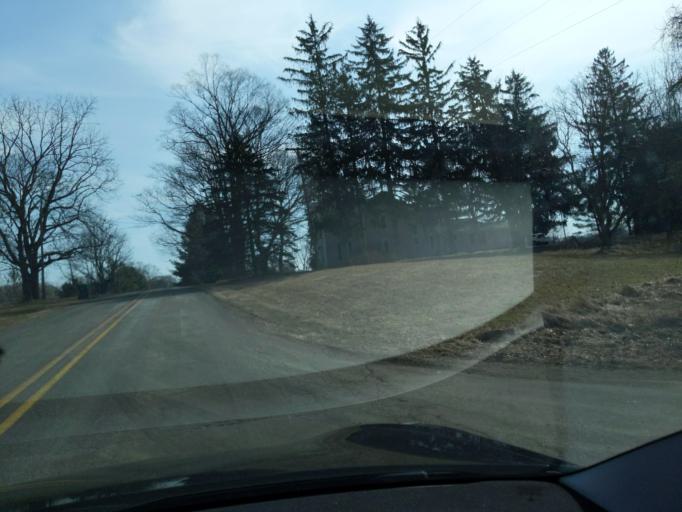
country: US
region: Michigan
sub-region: Ingham County
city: Williamston
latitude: 42.6588
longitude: -84.2965
